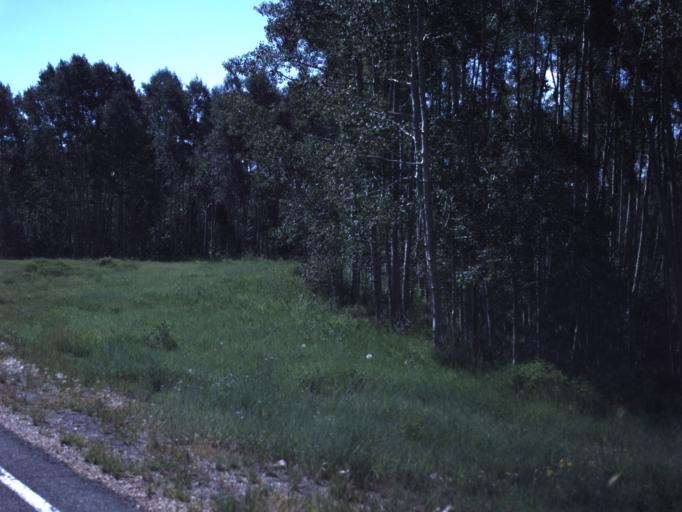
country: US
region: Utah
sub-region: Sanpete County
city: Fairview
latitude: 39.6553
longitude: -111.2925
